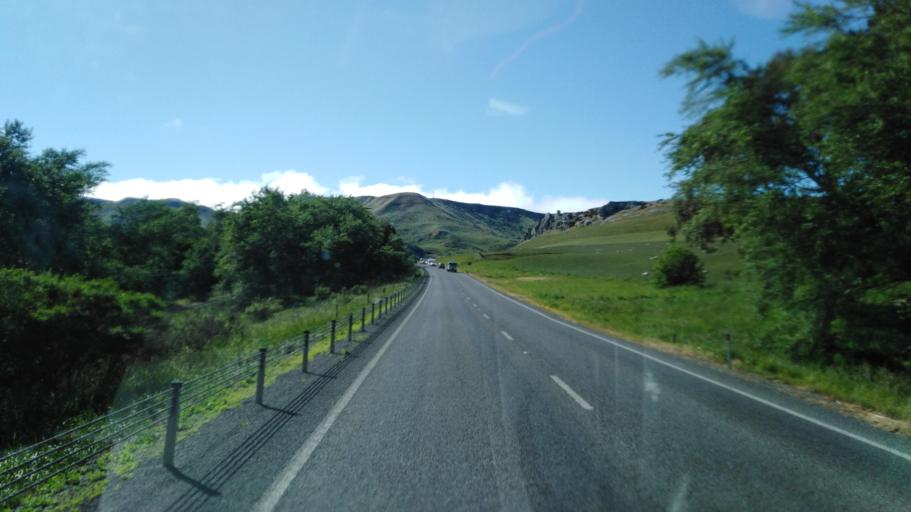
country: NZ
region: Canterbury
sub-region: Hurunui District
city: Amberley
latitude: -42.9786
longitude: 172.7108
